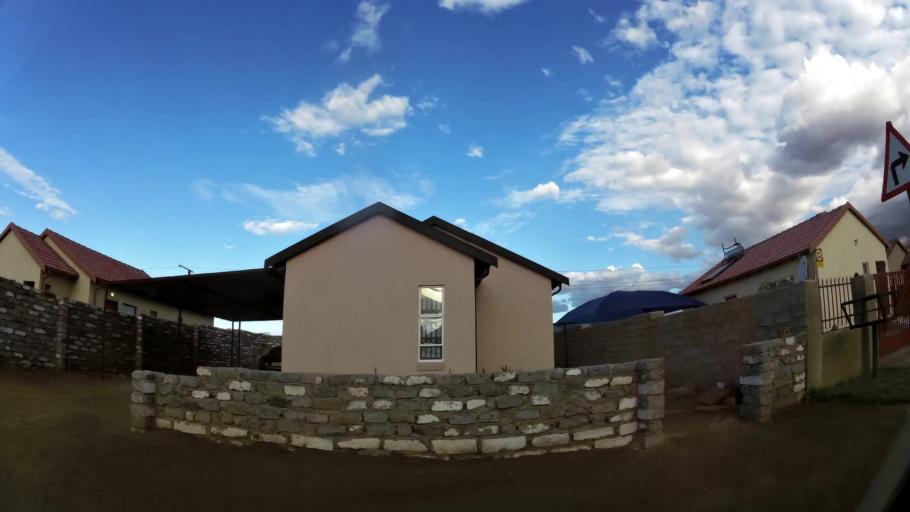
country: ZA
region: Limpopo
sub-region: Capricorn District Municipality
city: Polokwane
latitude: -23.9301
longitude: 29.4144
